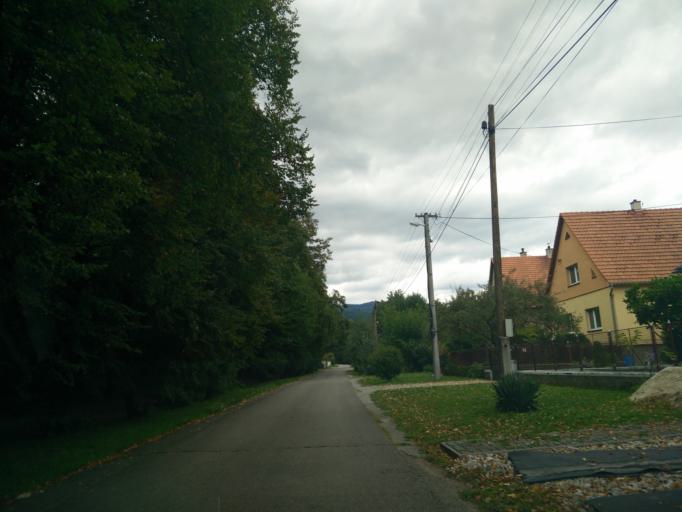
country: SK
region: Nitriansky
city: Novaky
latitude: 48.6383
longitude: 18.4857
